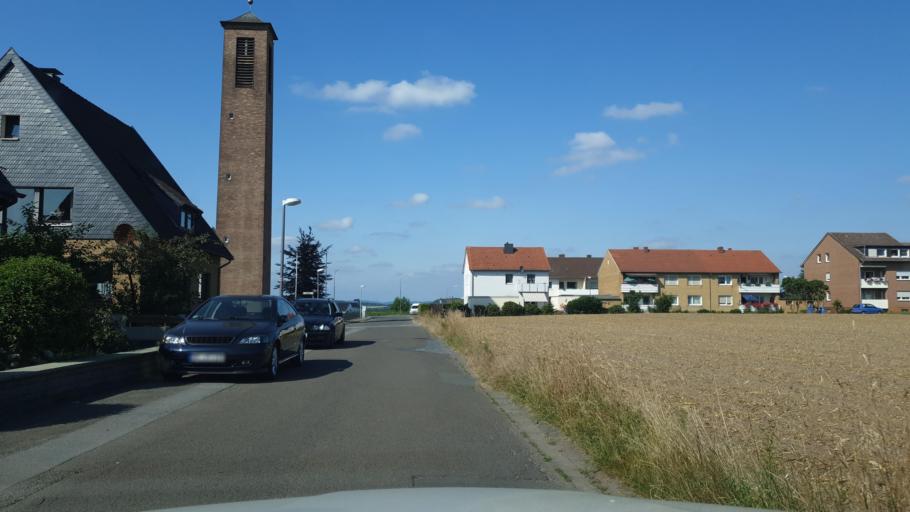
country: DE
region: North Rhine-Westphalia
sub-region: Regierungsbezirk Detmold
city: Hiddenhausen
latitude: 52.1276
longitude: 8.6213
